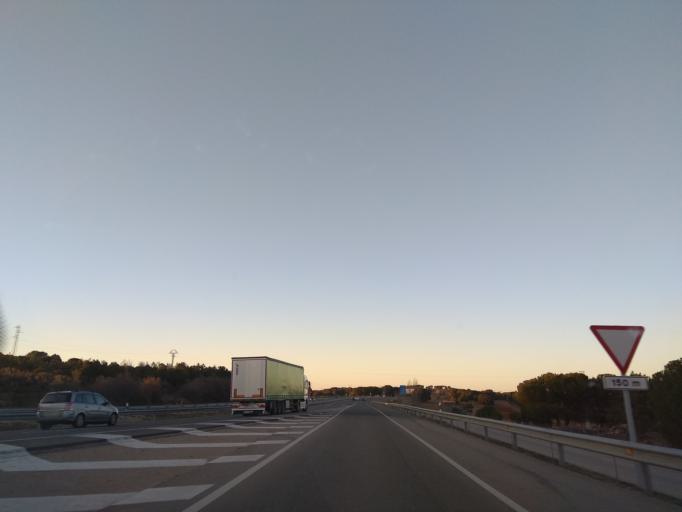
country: ES
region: Castille and Leon
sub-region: Provincia de Burgos
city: Aranda de Duero
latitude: 41.7144
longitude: -3.6882
